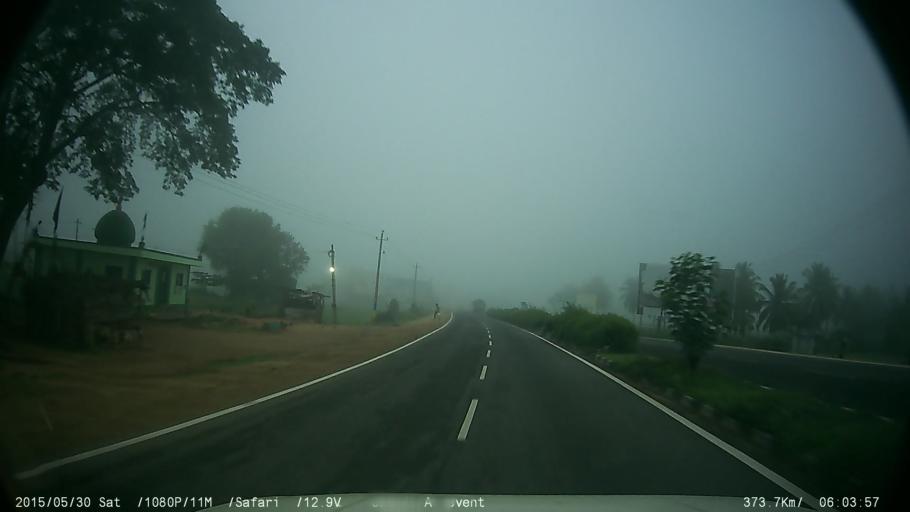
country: IN
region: Karnataka
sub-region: Mandya
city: Shrirangapattana
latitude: 12.4104
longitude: 76.6694
